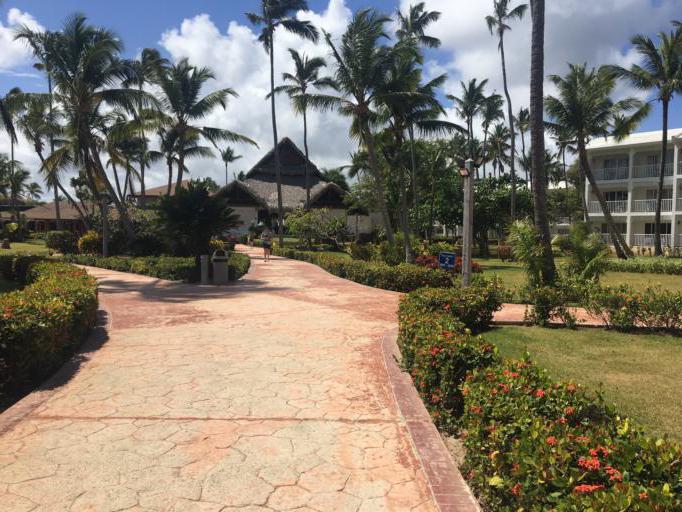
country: DO
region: San Juan
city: Punta Cana
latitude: 18.7089
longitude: -68.4431
